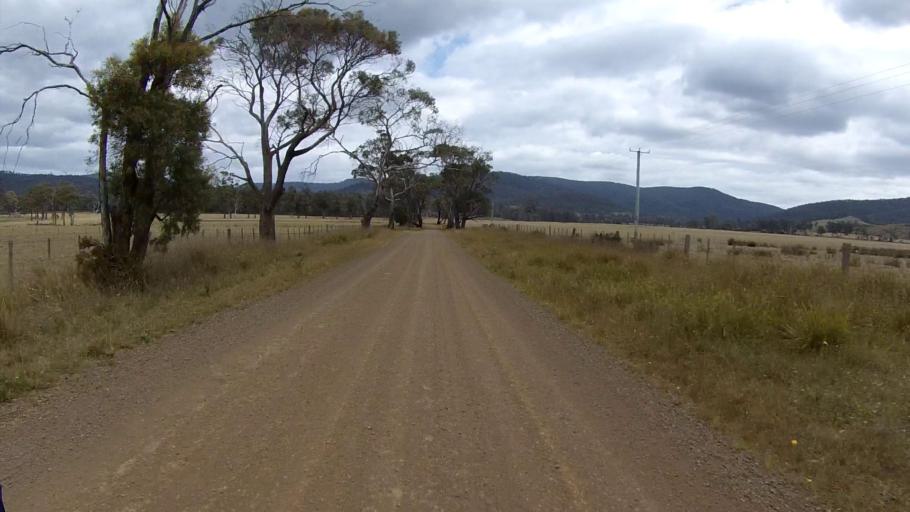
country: AU
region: Tasmania
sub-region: Sorell
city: Sorell
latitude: -42.6354
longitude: 147.9168
